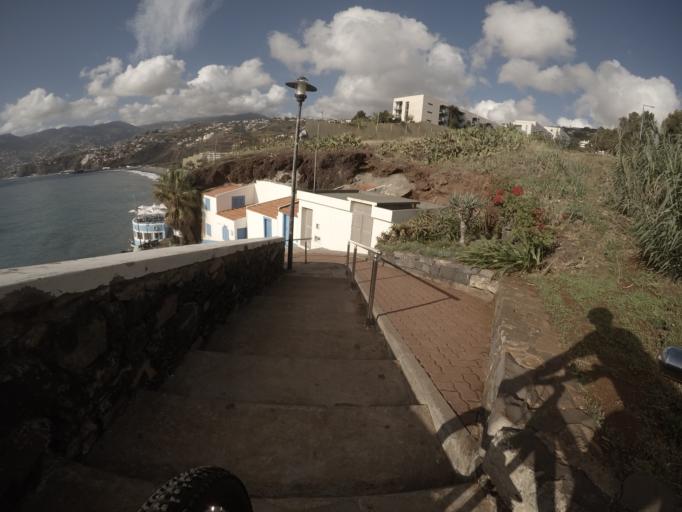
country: PT
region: Madeira
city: Camara de Lobos
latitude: 32.6350
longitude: -16.9474
